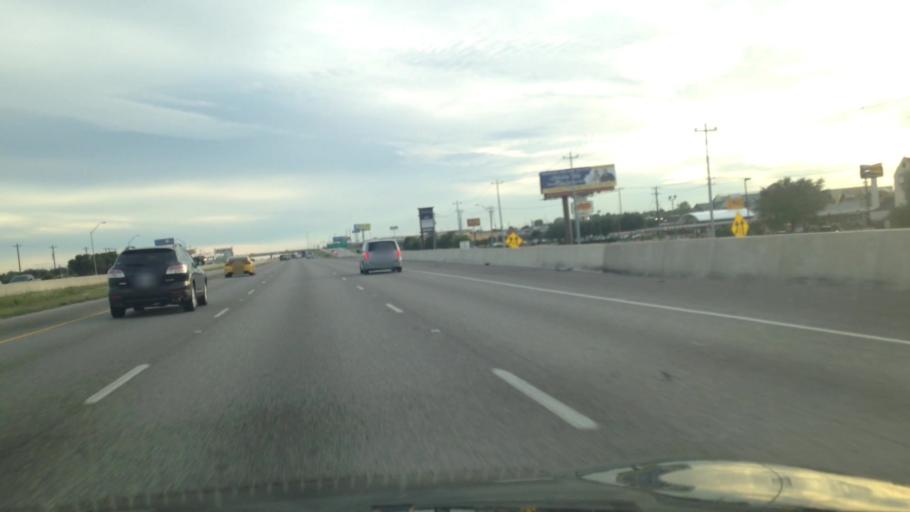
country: US
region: Texas
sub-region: Hays County
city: Buda
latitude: 30.0867
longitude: -97.8202
